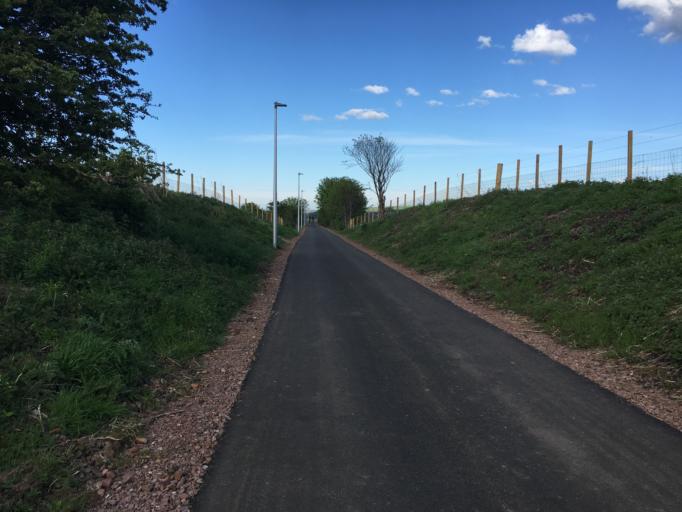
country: GB
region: Scotland
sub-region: Midlothian
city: Bonnyrigg
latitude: 55.9070
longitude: -3.1100
